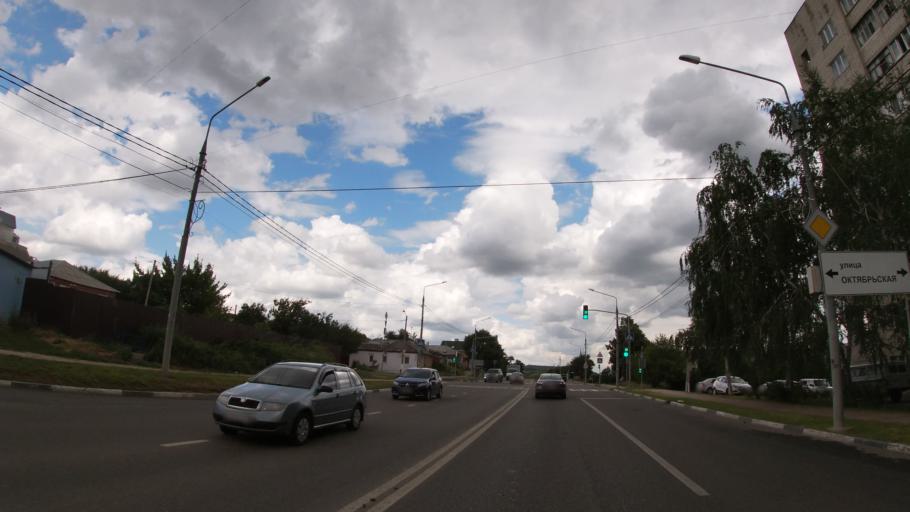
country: RU
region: Belgorod
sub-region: Belgorodskiy Rayon
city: Belgorod
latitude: 50.6024
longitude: 36.6097
